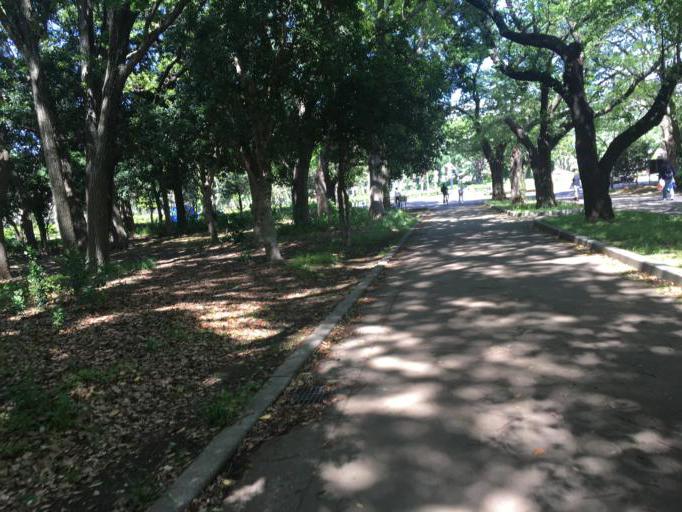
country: JP
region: Saitama
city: Wako
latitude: 35.7696
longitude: 139.6344
